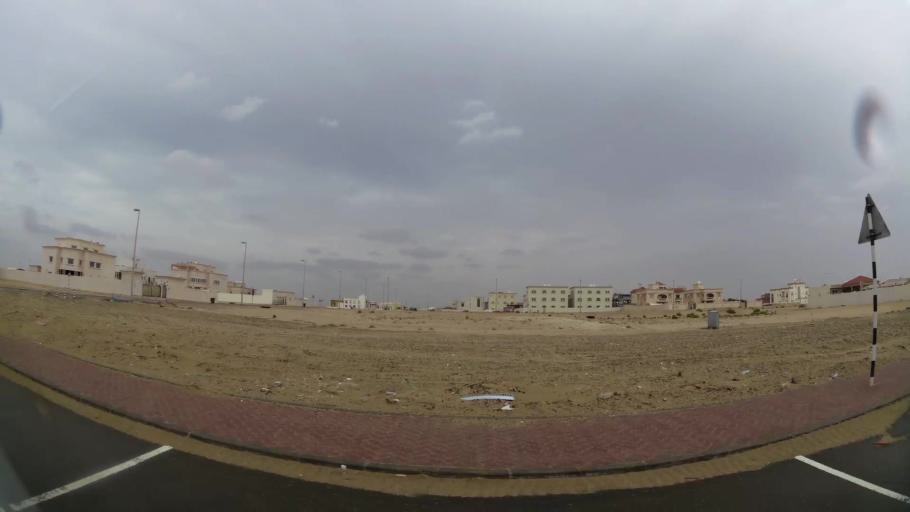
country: AE
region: Abu Dhabi
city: Abu Dhabi
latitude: 24.3623
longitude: 54.6202
